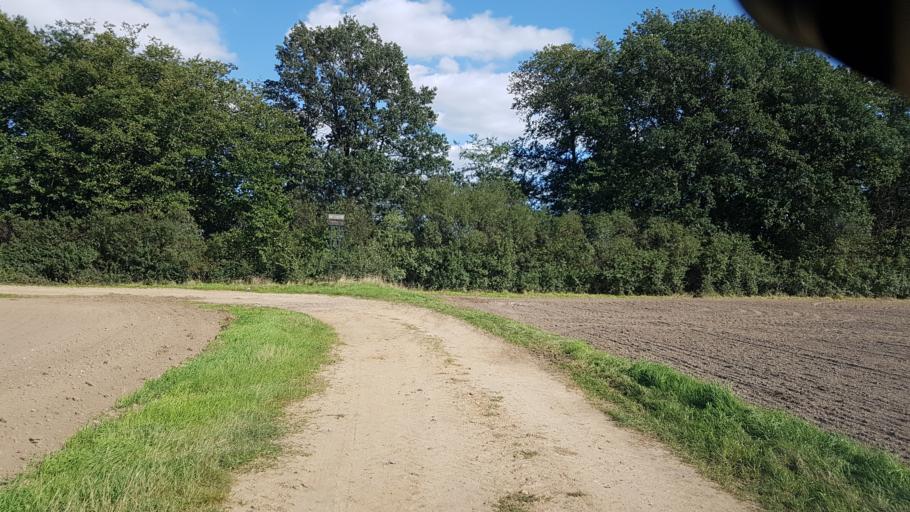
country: DE
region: Brandenburg
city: Sonnewalde
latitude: 51.6815
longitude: 13.6644
